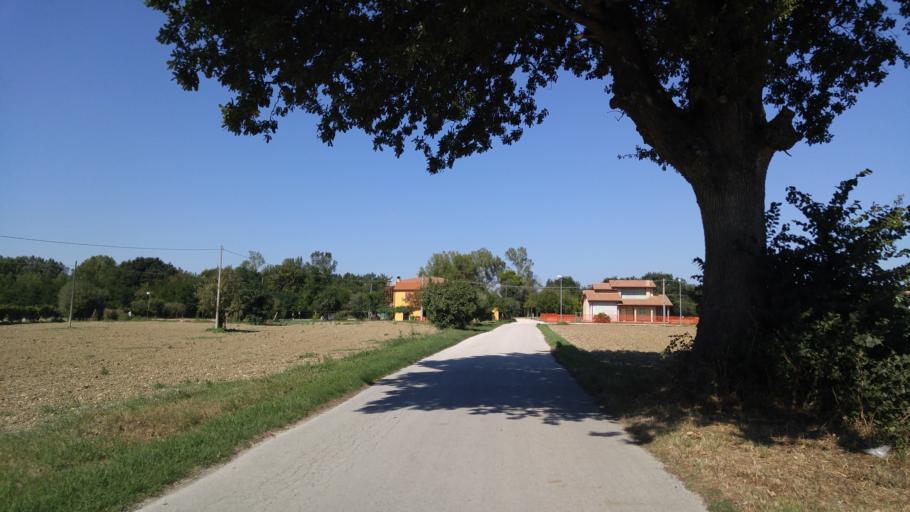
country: IT
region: The Marches
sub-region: Provincia di Pesaro e Urbino
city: Villanova
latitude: 43.7512
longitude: 12.9375
